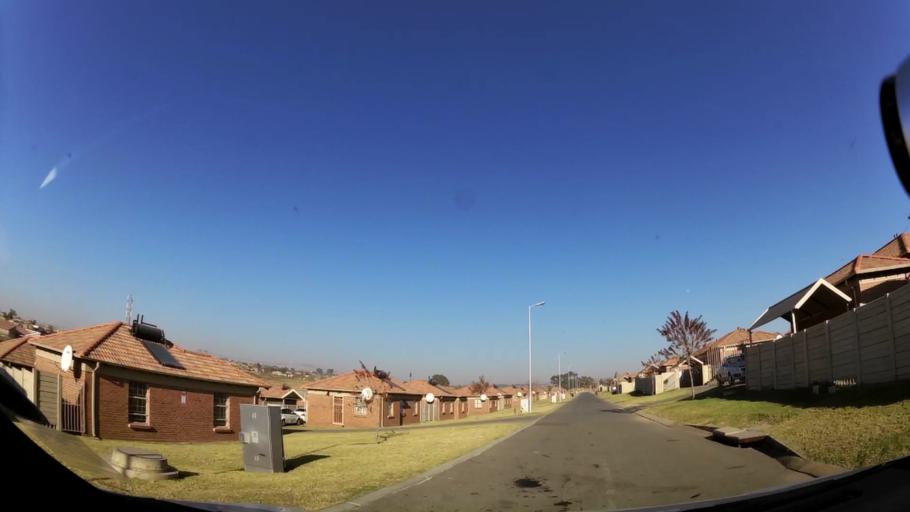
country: ZA
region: Gauteng
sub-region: City of Johannesburg Metropolitan Municipality
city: Midrand
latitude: -25.9102
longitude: 28.1102
